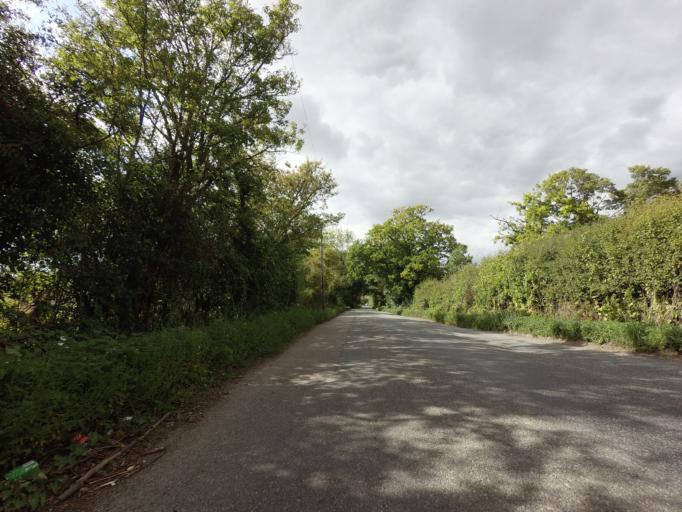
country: GB
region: England
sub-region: Kent
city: Paddock Wood
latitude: 51.1701
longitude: 0.4112
